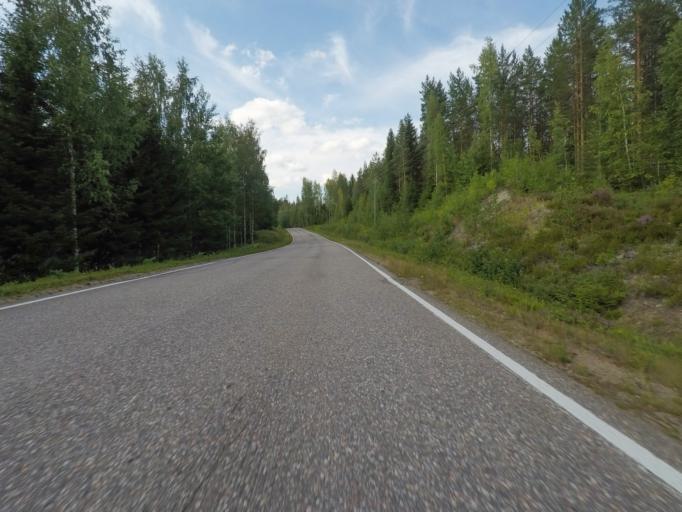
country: FI
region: Southern Savonia
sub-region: Savonlinna
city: Sulkava
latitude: 61.7327
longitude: 28.2100
